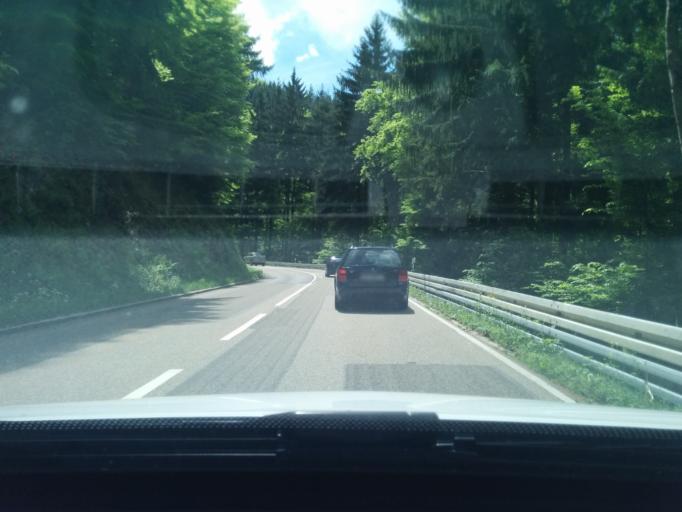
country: DE
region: Baden-Wuerttemberg
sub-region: Freiburg Region
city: Horben
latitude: 47.9273
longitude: 7.8779
